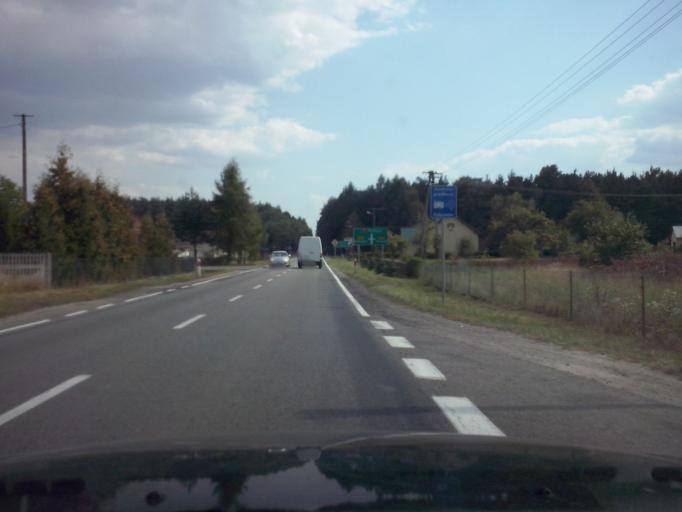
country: PL
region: Subcarpathian Voivodeship
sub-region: Powiat nizanski
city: Bieliny
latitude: 50.3999
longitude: 22.2949
